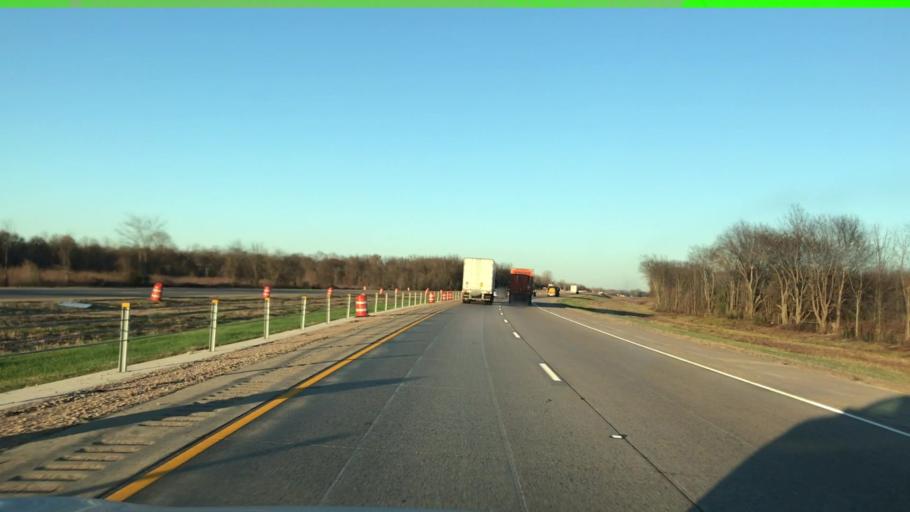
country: US
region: Arkansas
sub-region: Miller County
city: Texarkana
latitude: 33.5841
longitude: -93.8412
